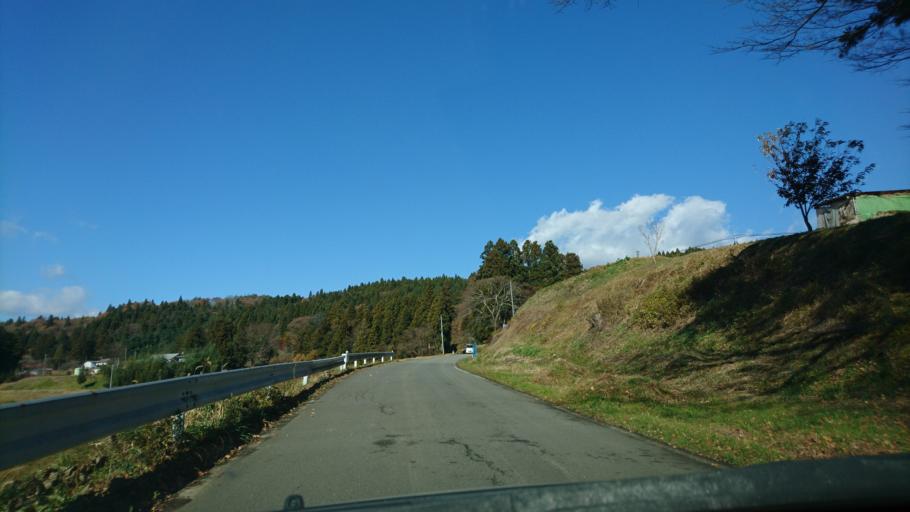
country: JP
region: Iwate
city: Ichinoseki
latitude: 38.9995
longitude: 141.0858
